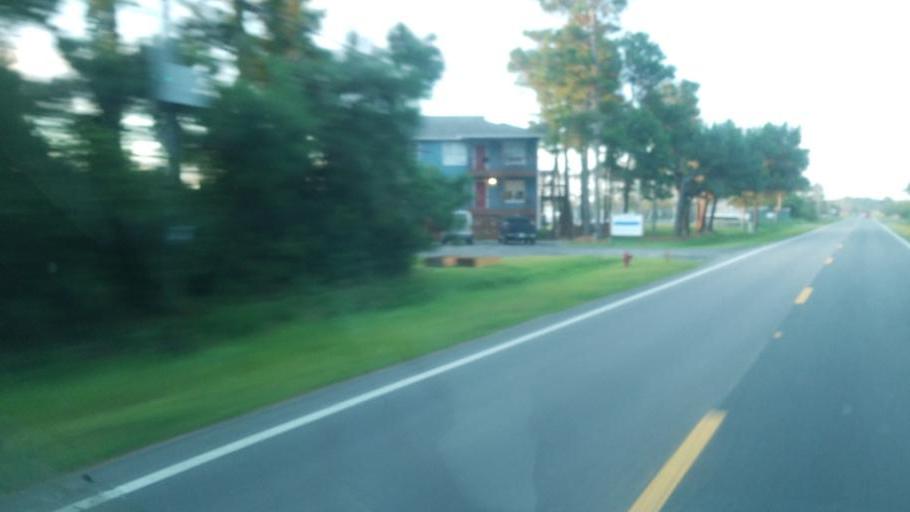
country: US
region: North Carolina
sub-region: Dare County
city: Wanchese
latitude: 35.8624
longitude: -75.6478
